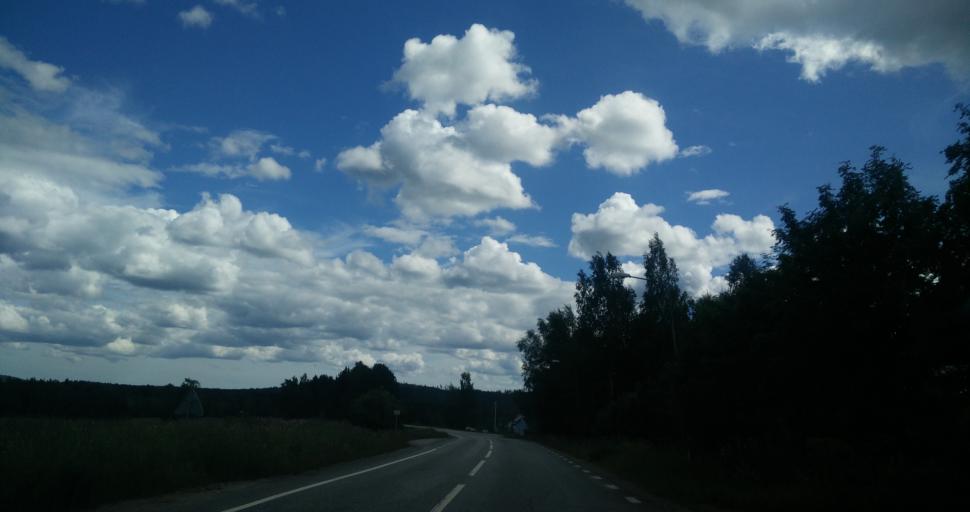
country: SE
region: Gaevleborg
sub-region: Nordanstigs Kommun
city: Bergsjoe
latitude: 62.0582
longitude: 16.8366
